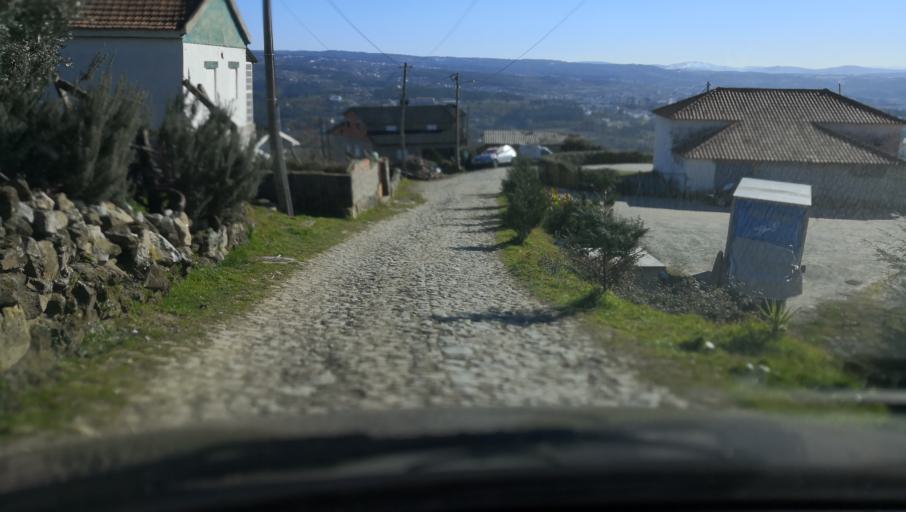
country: PT
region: Vila Real
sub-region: Vila Real
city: Vila Real
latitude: 41.3309
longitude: -7.7556
